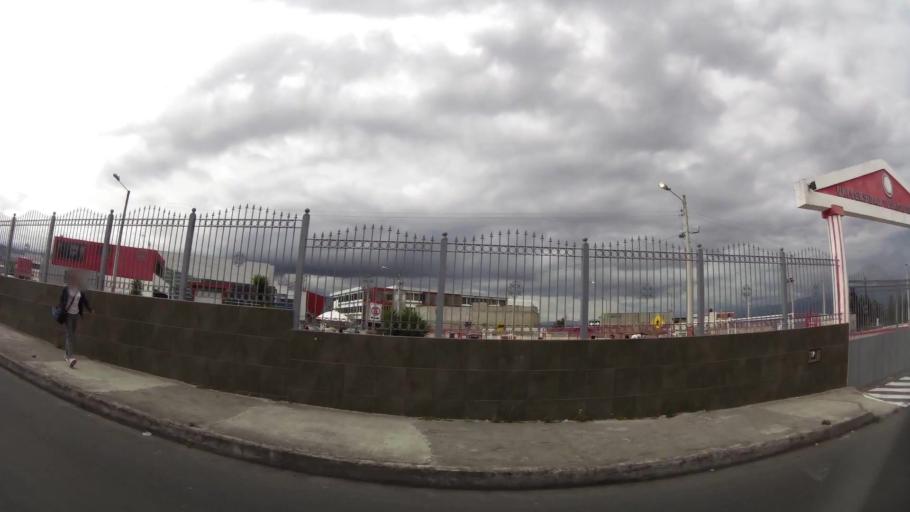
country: EC
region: Tungurahua
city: Ambato
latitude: -1.2707
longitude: -78.6242
